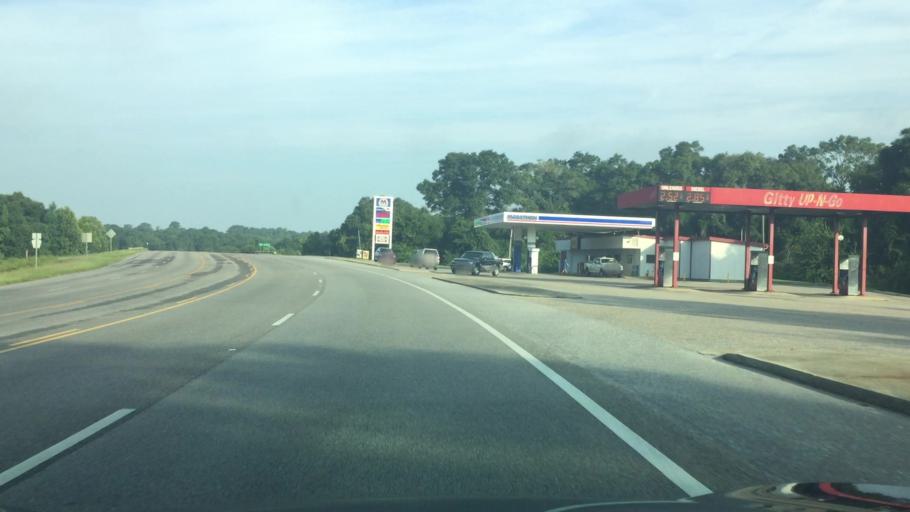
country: US
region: Alabama
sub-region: Covington County
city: Andalusia
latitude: 31.3471
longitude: -86.5267
